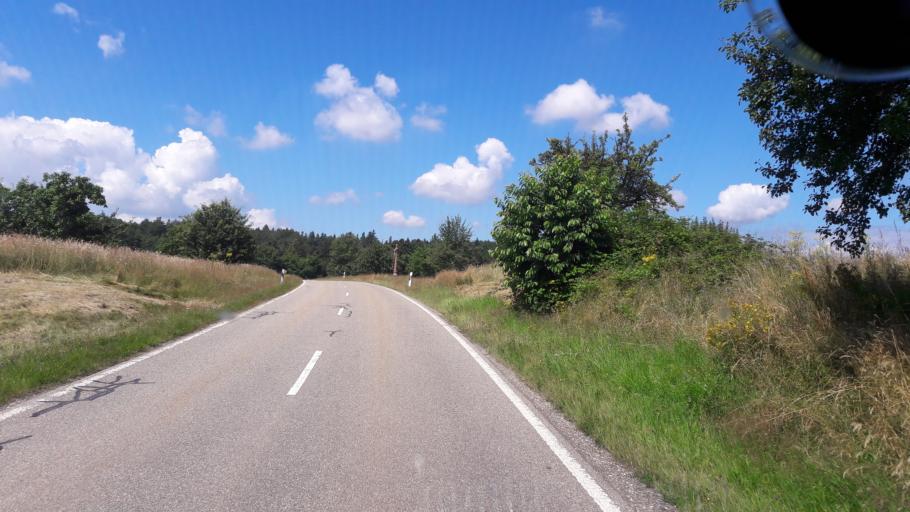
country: DE
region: Baden-Wuerttemberg
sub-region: Karlsruhe Region
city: Malsch
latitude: 48.8718
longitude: 8.3822
